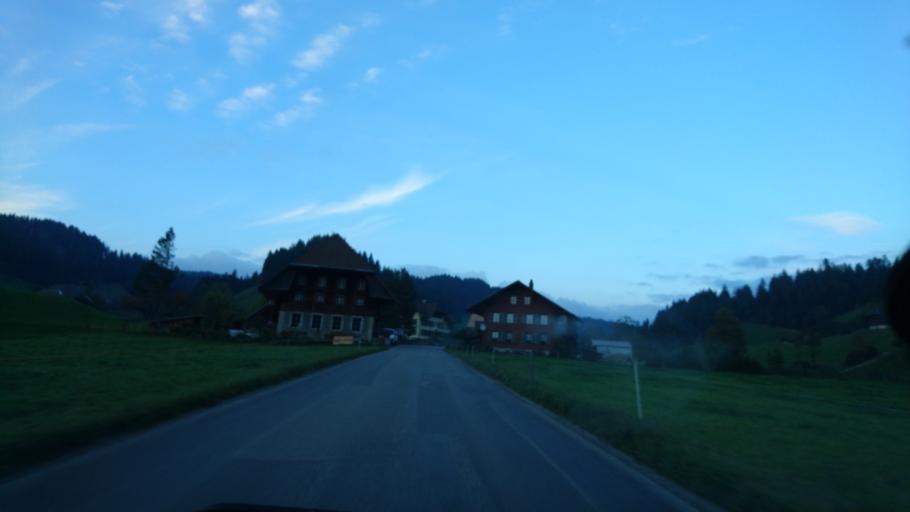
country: CH
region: Bern
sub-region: Emmental District
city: Trub
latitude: 46.9488
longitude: 7.8900
